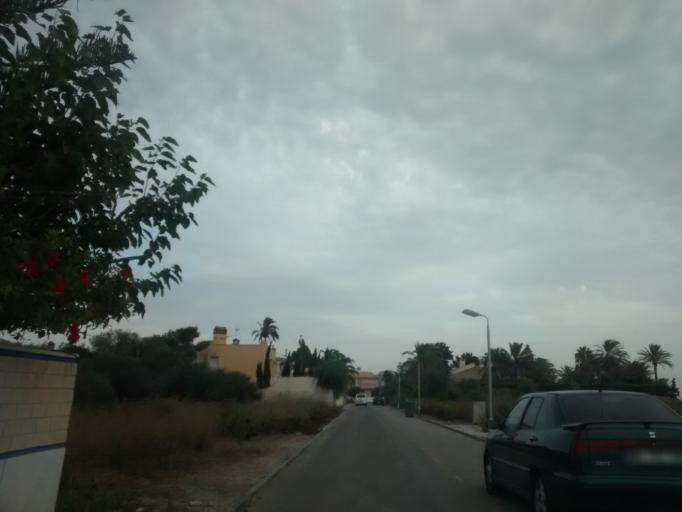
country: ES
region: Murcia
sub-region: Murcia
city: San Pedro del Pinatar
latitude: 37.7785
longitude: -0.7540
